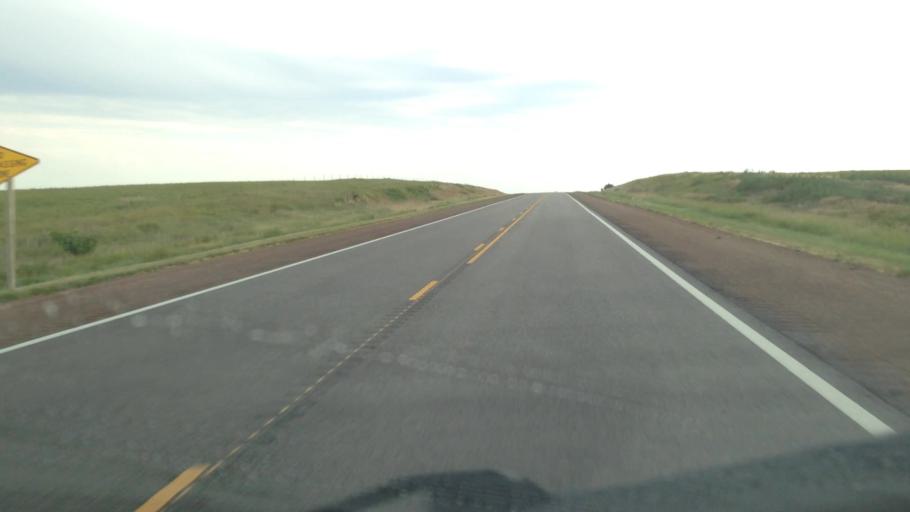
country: US
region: Kansas
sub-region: Coffey County
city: Burlington
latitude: 38.0504
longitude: -95.7391
